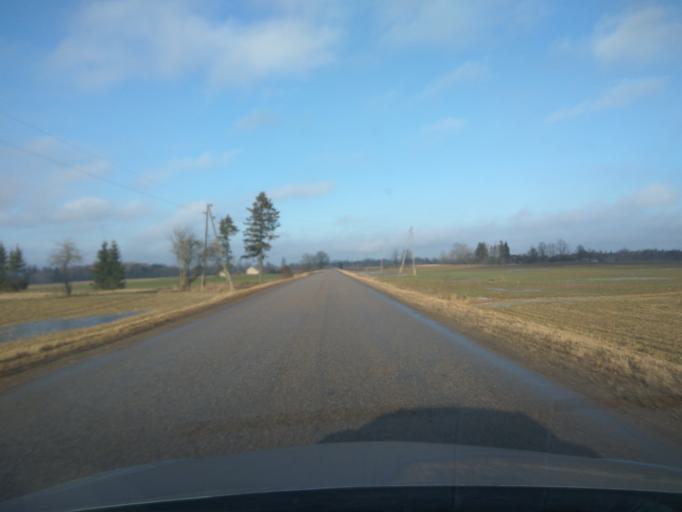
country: LV
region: Saldus Rajons
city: Saldus
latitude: 56.8389
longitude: 22.3789
